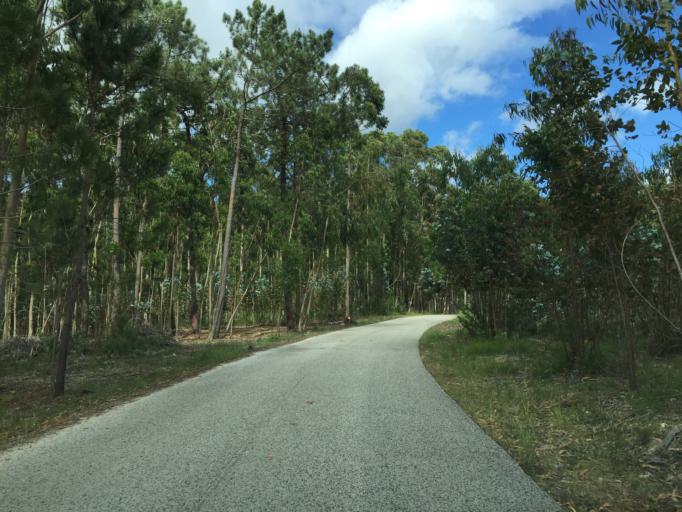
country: PT
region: Coimbra
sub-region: Figueira da Foz
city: Tavarede
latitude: 40.2111
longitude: -8.8371
